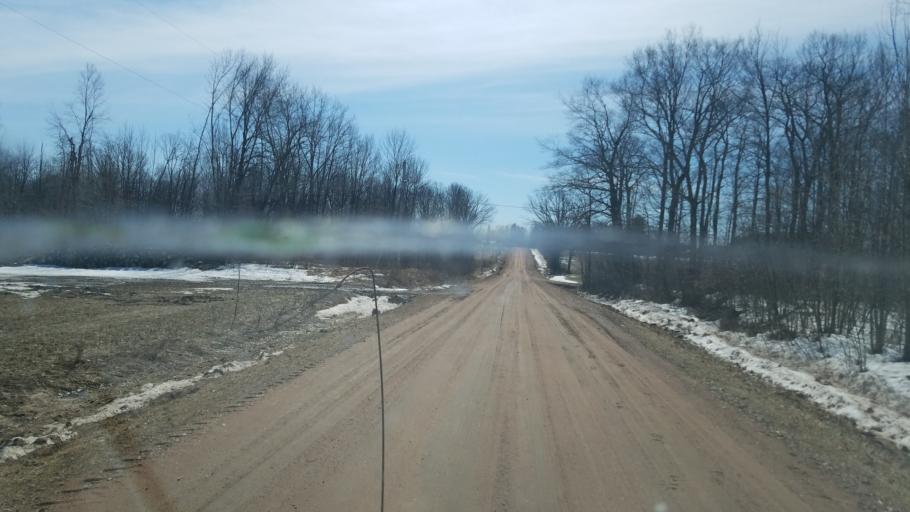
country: US
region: Wisconsin
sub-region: Clark County
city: Loyal
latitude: 44.6307
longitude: -90.4072
